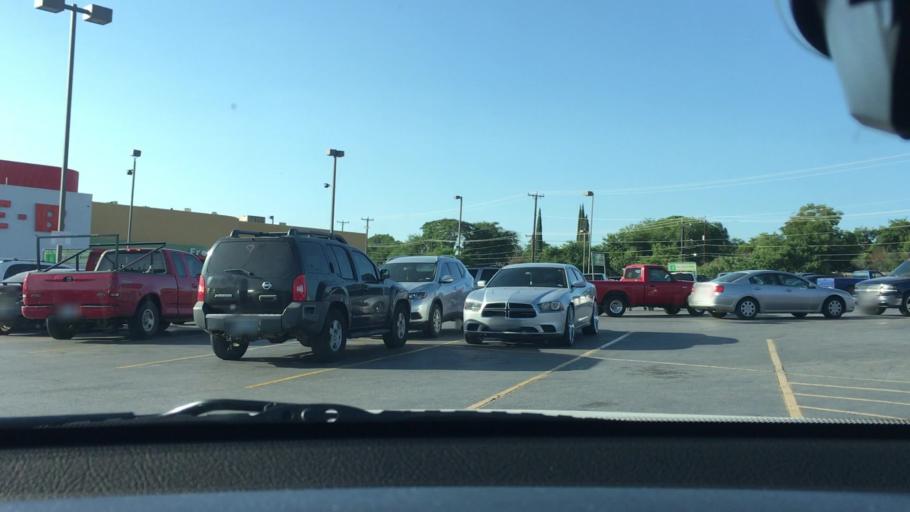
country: US
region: Texas
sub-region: Bexar County
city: Live Oak
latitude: 29.5688
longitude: -98.3864
